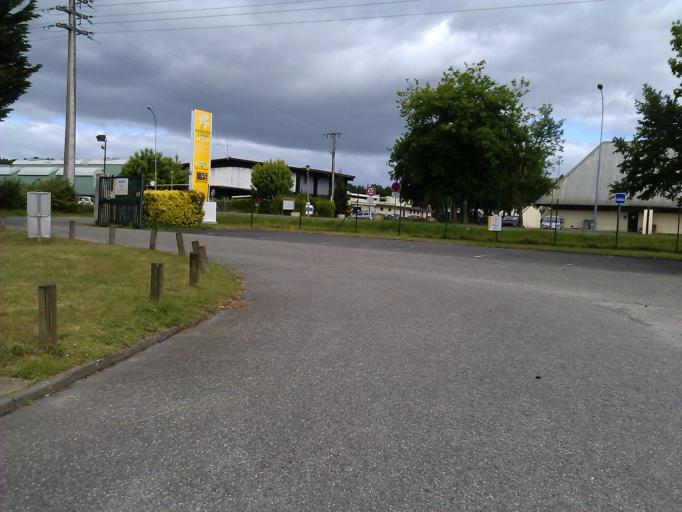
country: FR
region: Aquitaine
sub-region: Departement de la Gironde
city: Cestas
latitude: 44.7592
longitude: -0.6836
